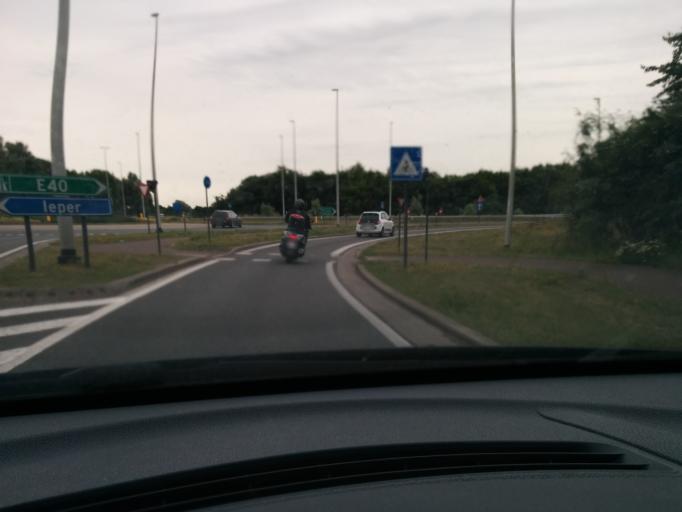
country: BE
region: Flanders
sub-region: Provincie West-Vlaanderen
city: Veurne
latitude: 51.0558
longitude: 2.6673
